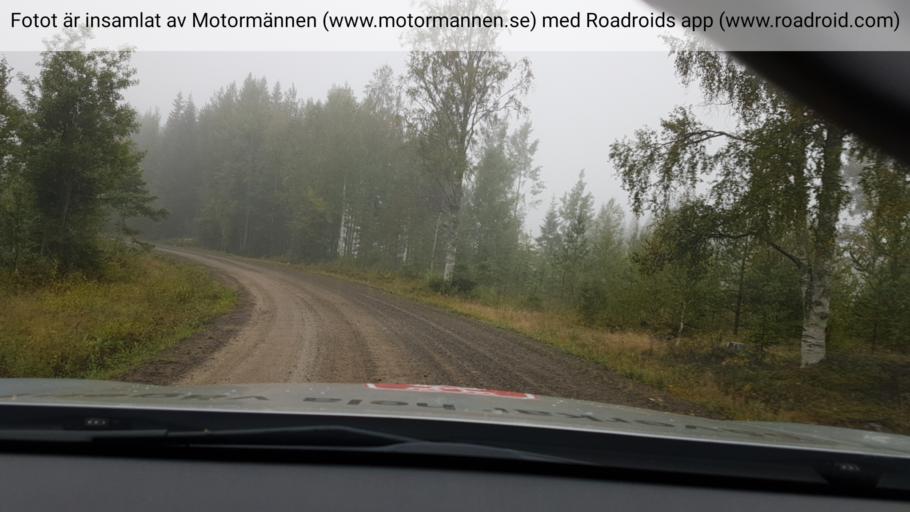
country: SE
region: Vaesterbotten
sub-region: Robertsfors Kommun
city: Robertsfors
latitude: 64.2356
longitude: 20.5649
